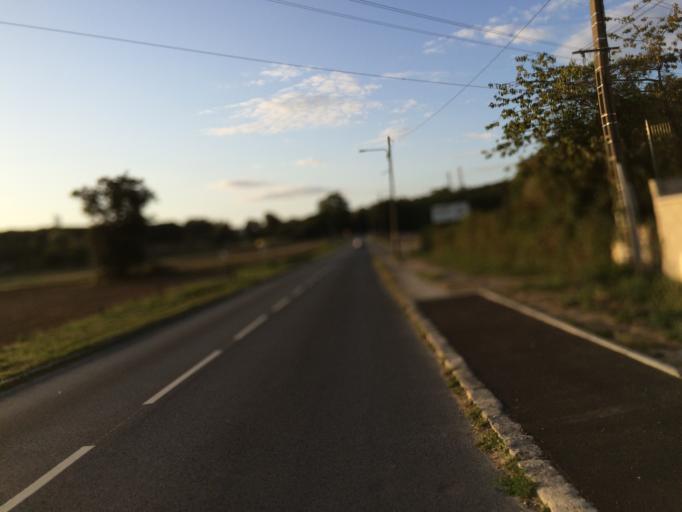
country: FR
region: Ile-de-France
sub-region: Departement de l'Essonne
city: Nozay
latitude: 48.6589
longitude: 2.2074
